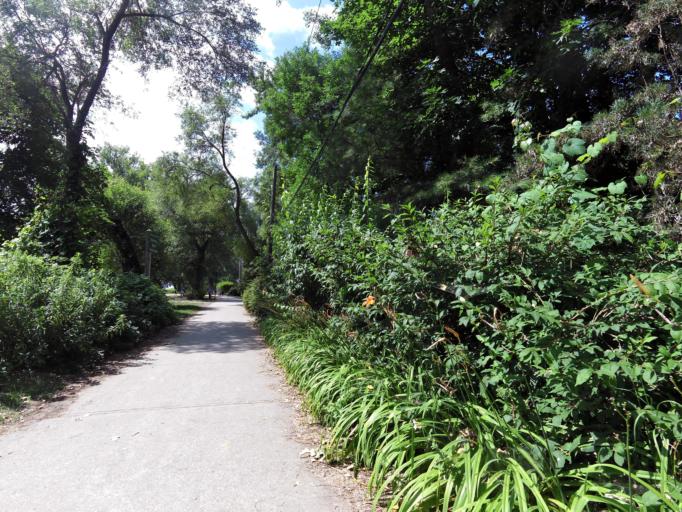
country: CA
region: Ontario
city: Toronto
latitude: 43.6316
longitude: -79.3538
